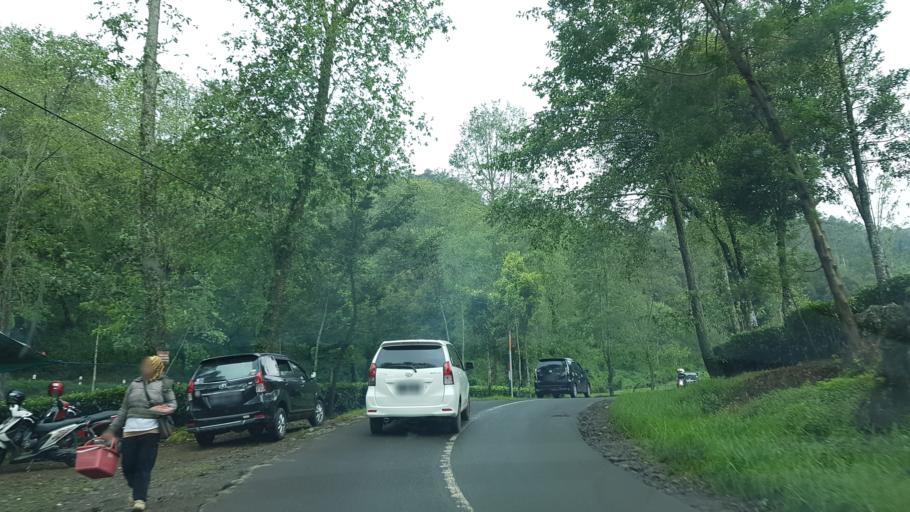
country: ID
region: West Java
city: Banjar
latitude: -7.1508
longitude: 107.3819
